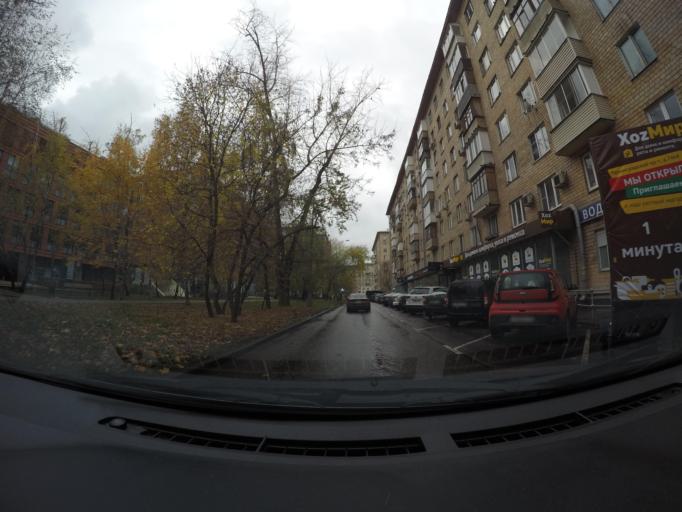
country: RU
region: Moscow
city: Sokol
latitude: 55.8061
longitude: 37.5195
